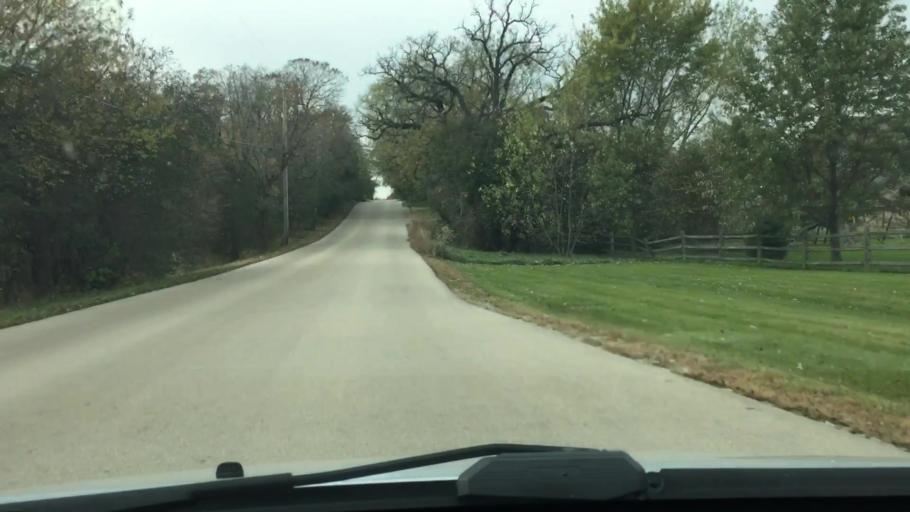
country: US
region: Wisconsin
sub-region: Waukesha County
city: North Prairie
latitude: 42.9304
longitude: -88.4287
